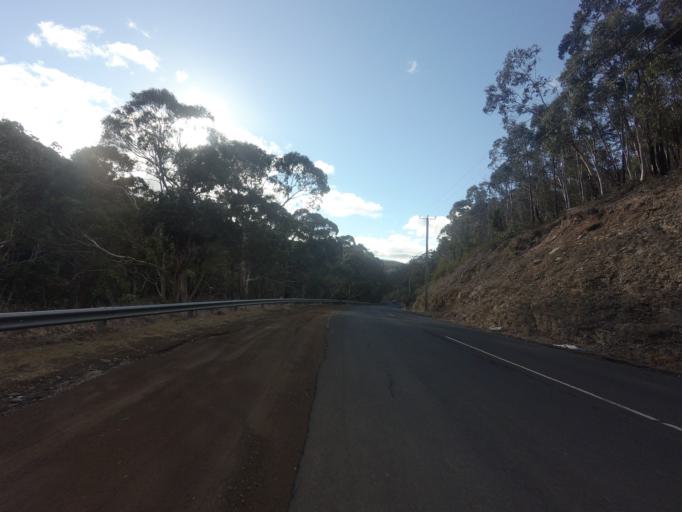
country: AU
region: Tasmania
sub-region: Glenorchy
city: Berriedale
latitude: -42.8261
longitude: 147.2090
